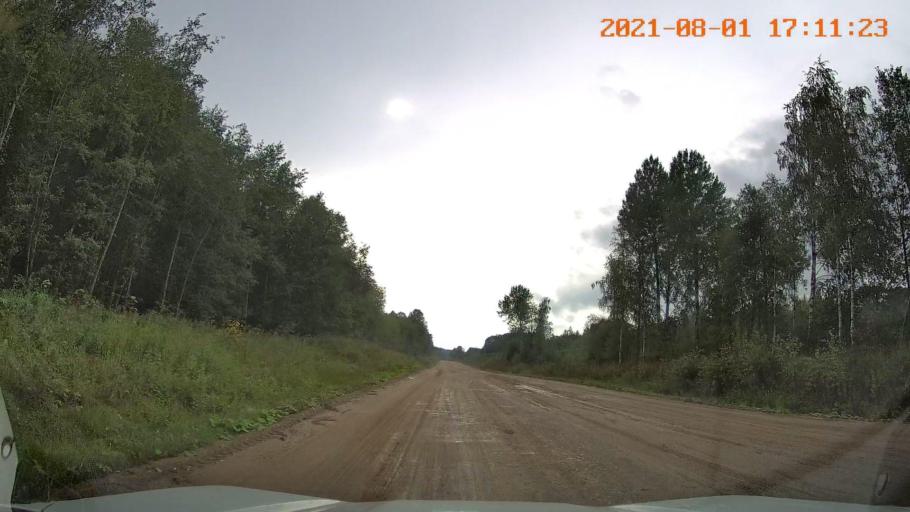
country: RU
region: Vologda
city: Vytegra
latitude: 61.0002
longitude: 36.2704
